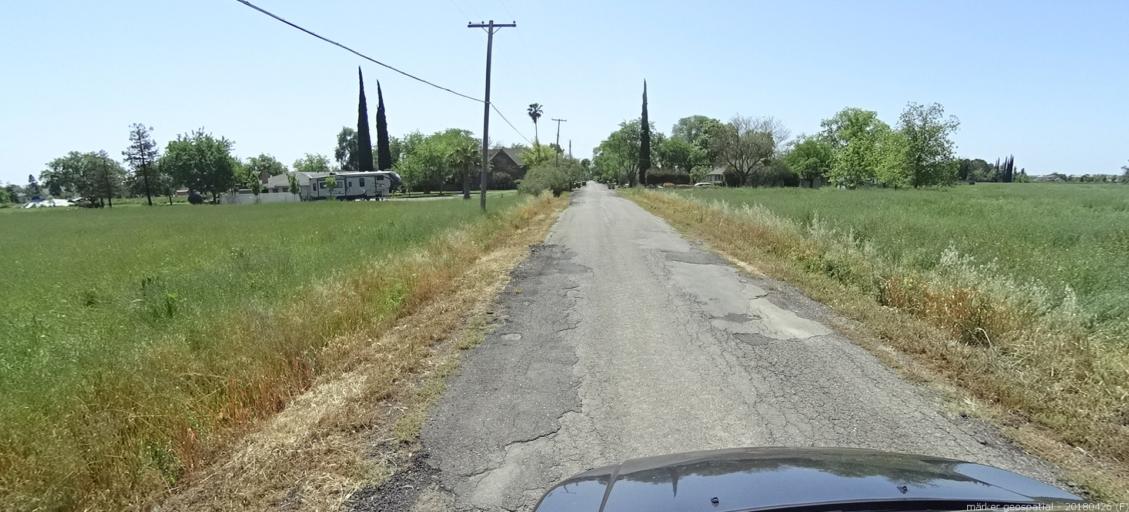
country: US
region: California
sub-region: Yolo County
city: West Sacramento
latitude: 38.5341
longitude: -121.5617
